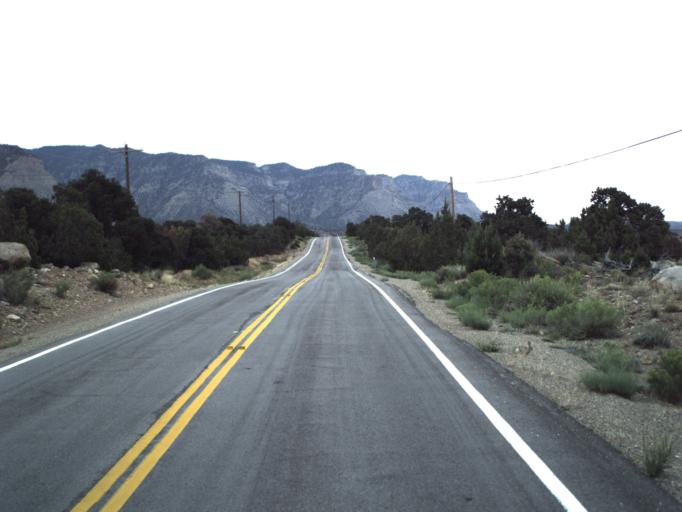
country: US
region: Utah
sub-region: Carbon County
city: East Carbon City
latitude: 39.5320
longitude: -110.4021
